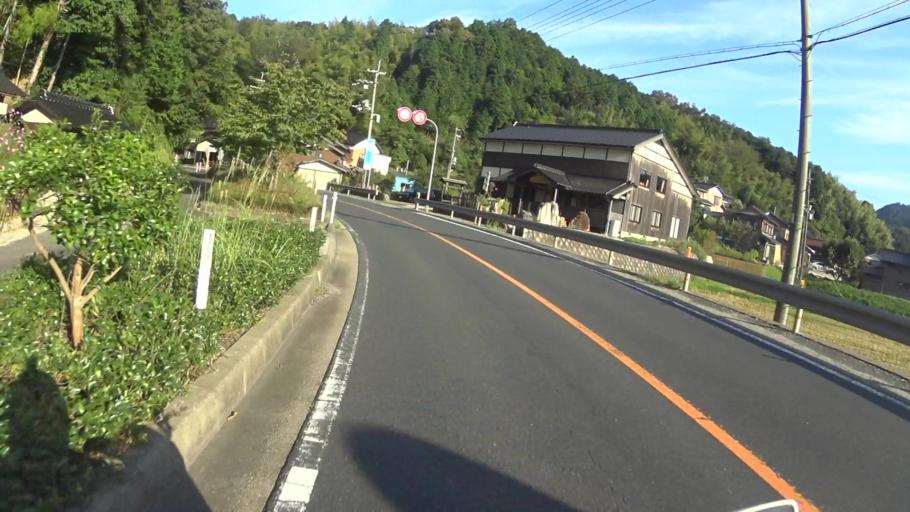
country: JP
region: Hyogo
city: Toyooka
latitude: 35.5942
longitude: 134.9061
